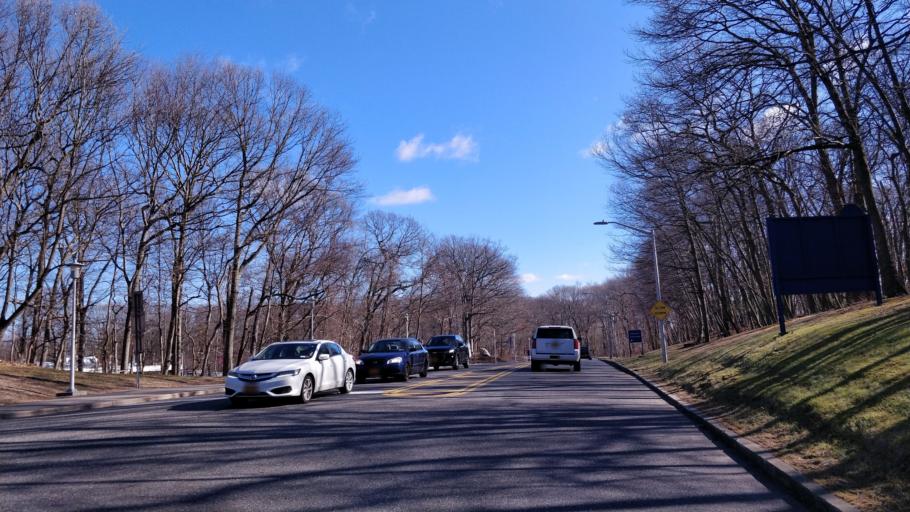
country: US
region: New York
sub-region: Suffolk County
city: Stony Brook
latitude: 40.9020
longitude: -73.1218
